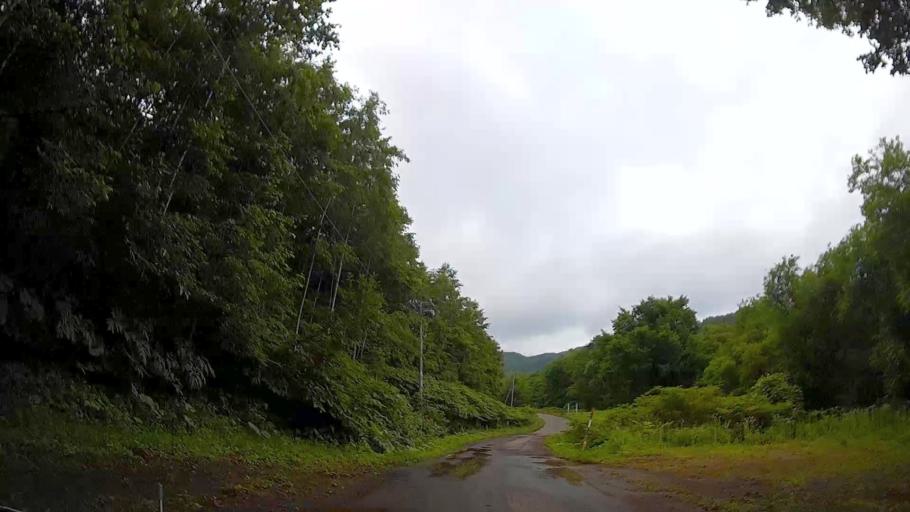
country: JP
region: Hokkaido
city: Nanae
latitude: 42.0724
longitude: 140.5206
